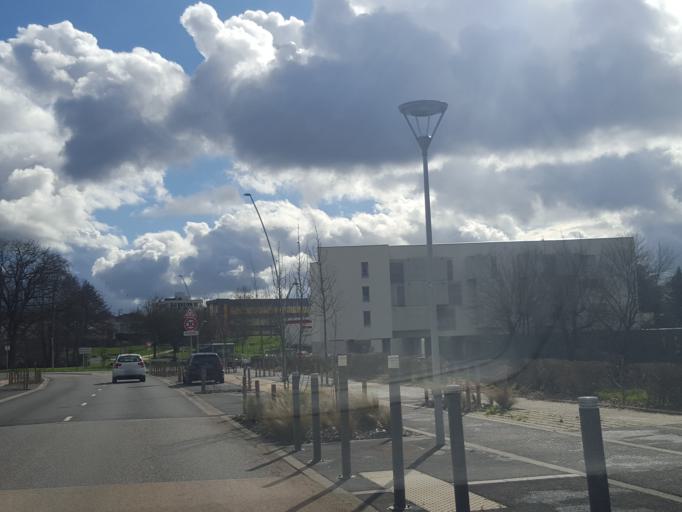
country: FR
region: Pays de la Loire
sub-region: Departement de la Vendee
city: La Roche-sur-Yon
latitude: 46.6791
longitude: -1.4406
